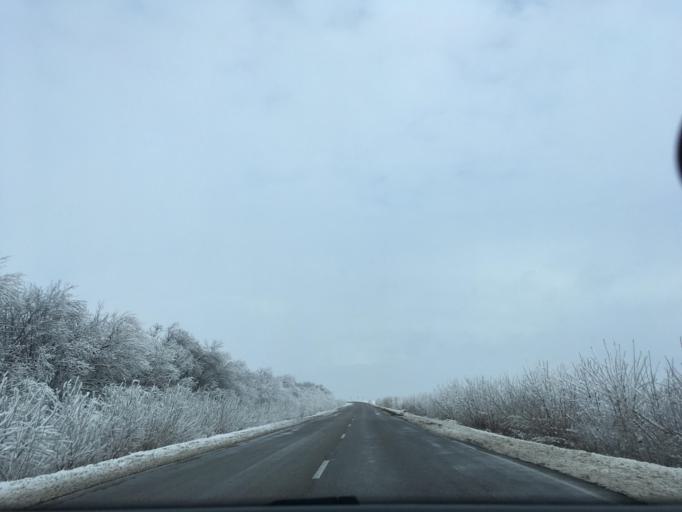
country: UA
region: Luhansk
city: Lozno-Oleksandrivka
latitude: 49.9956
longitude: 39.0352
